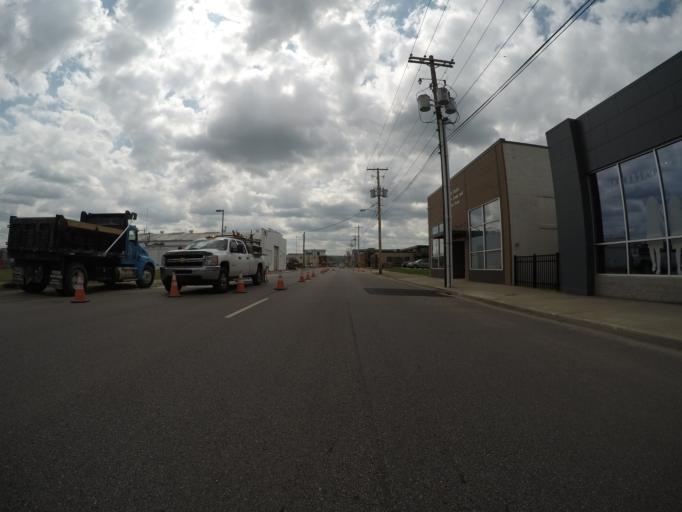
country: US
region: West Virginia
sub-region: Kanawha County
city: Charleston
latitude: 38.3605
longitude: -81.6477
